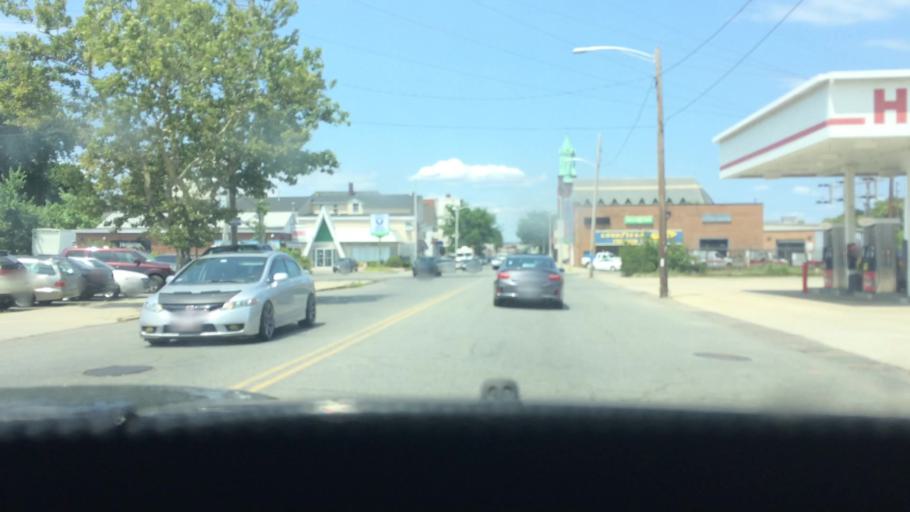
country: US
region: Massachusetts
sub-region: Essex County
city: Lawrence
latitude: 42.6944
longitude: -71.1621
